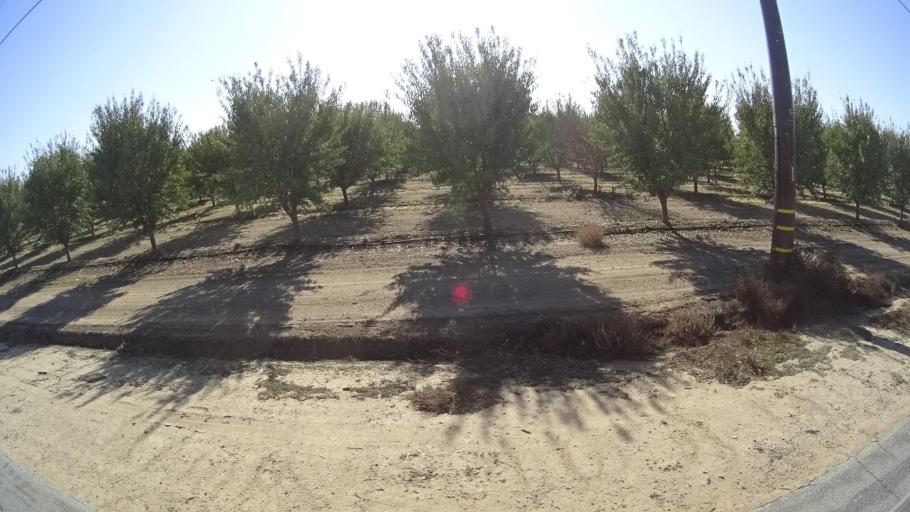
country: US
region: California
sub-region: Kern County
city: McFarland
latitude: 35.7178
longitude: -119.1996
